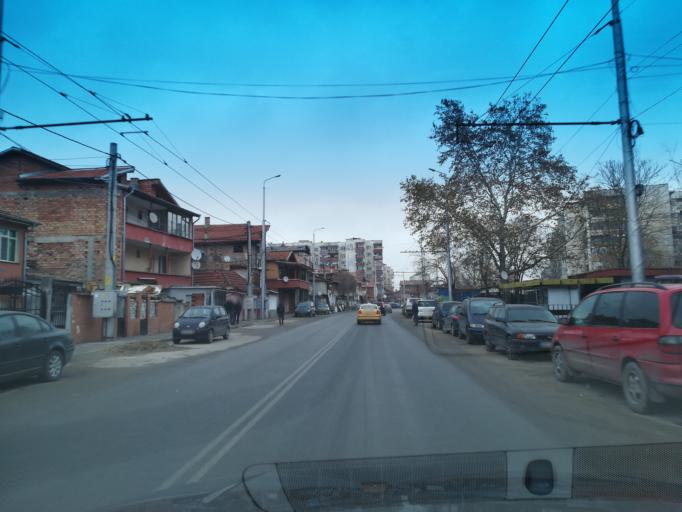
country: BG
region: Plovdiv
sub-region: Obshtina Plovdiv
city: Plovdiv
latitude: 42.1540
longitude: 24.7872
